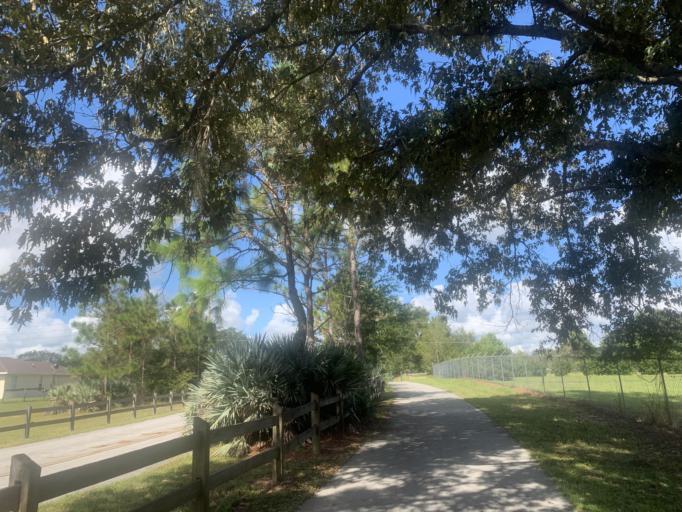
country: US
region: Florida
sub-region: Marion County
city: Silver Springs Shores
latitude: 29.1568
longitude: -82.0460
